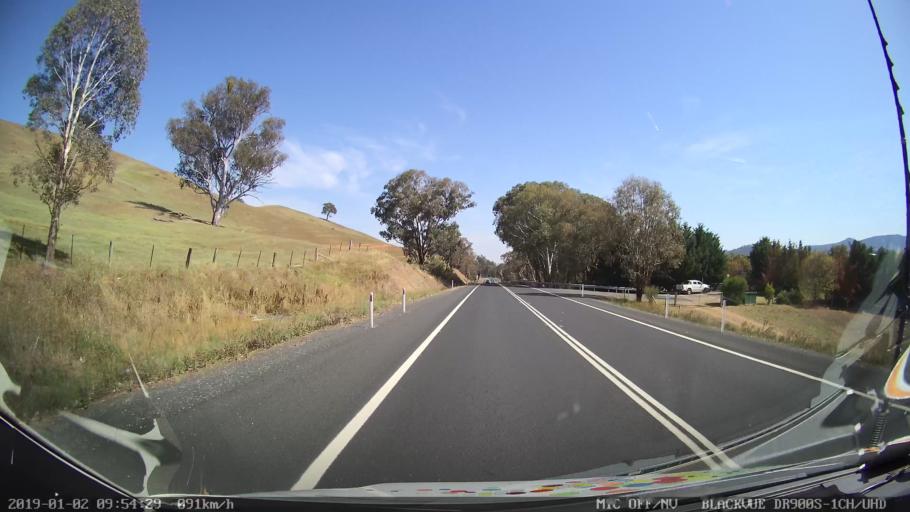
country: AU
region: New South Wales
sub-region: Tumut Shire
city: Tumut
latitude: -35.2345
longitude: 148.1959
